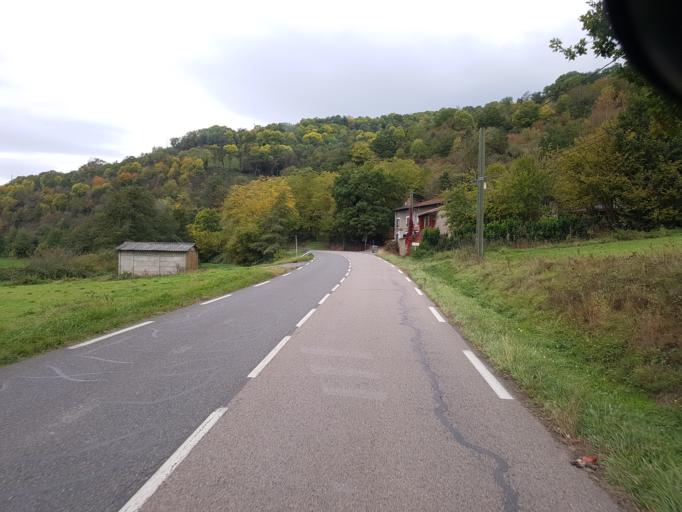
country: FR
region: Rhone-Alpes
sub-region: Departement du Rhone
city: Sainte-Foy-l'Argentiere
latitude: 45.7223
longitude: 4.4909
